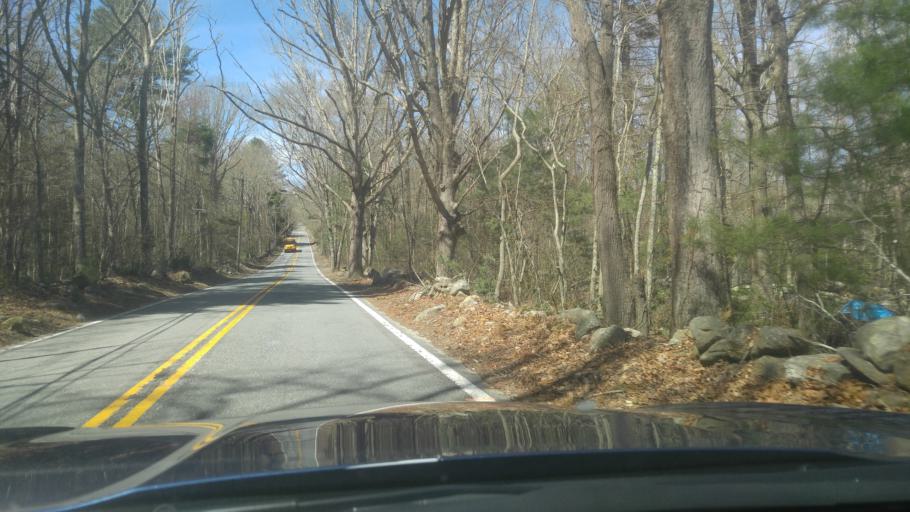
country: US
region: Rhode Island
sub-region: Washington County
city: Hope Valley
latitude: 41.5817
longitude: -71.7569
